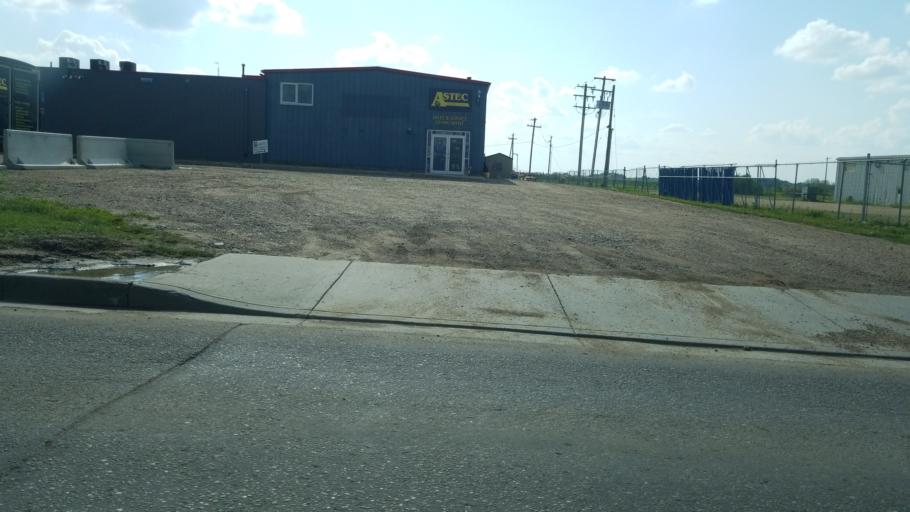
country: CA
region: Saskatchewan
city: Lloydminster
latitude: 53.2792
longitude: -110.0340
